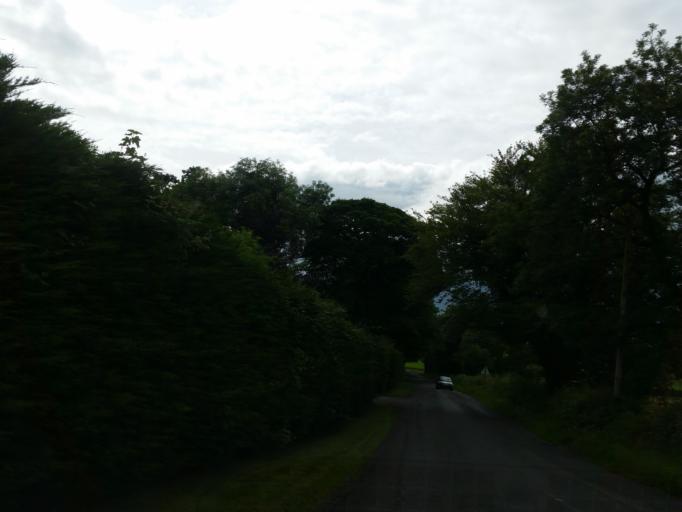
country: IE
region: Ulster
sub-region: County Monaghan
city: Clones
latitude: 54.1954
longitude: -7.2527
